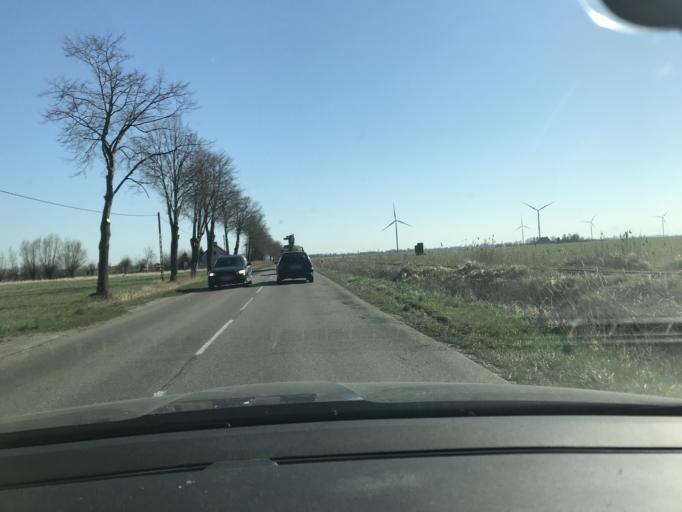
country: PL
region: Pomeranian Voivodeship
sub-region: Powiat nowodworski
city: Nowy Dwor Gdanski
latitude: 54.2646
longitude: 19.1359
